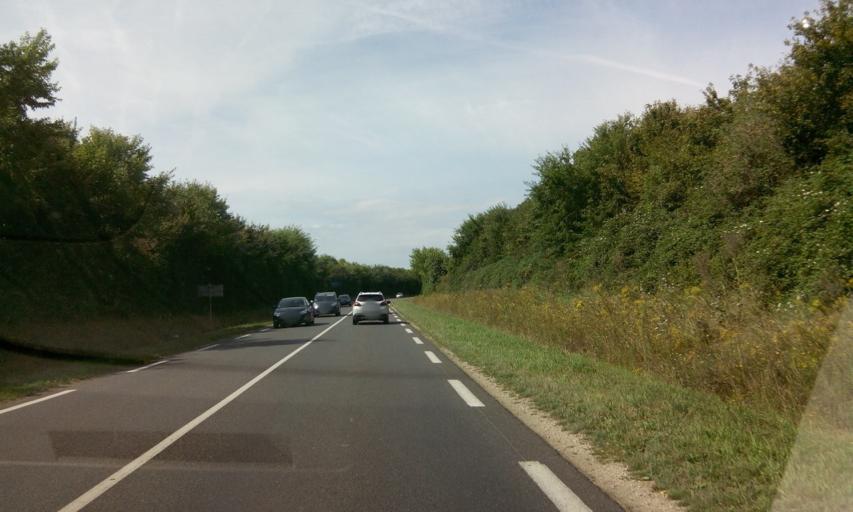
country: FR
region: Poitou-Charentes
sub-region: Departement de la Vienne
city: Civray
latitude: 46.1610
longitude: 0.2956
